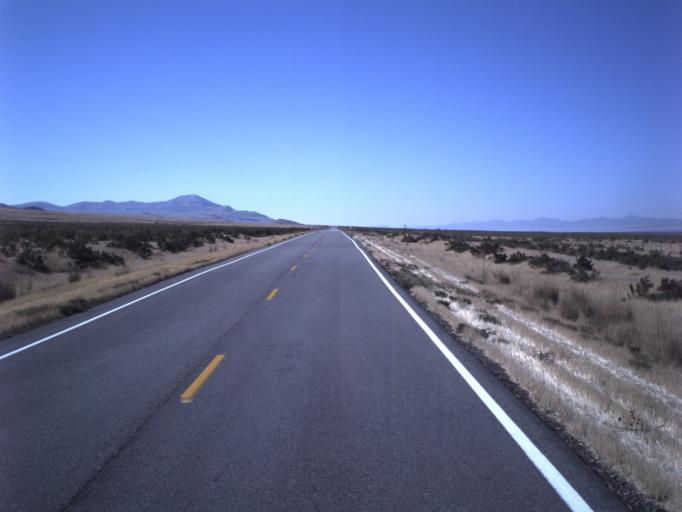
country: US
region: Utah
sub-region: Tooele County
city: Grantsville
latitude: 40.6592
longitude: -112.6798
